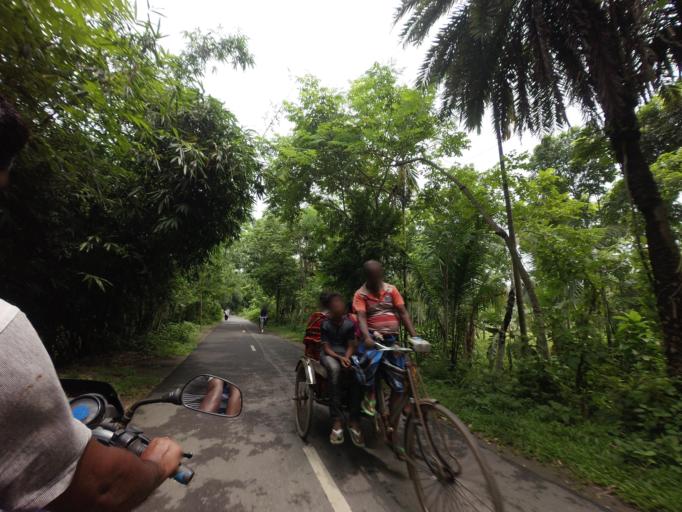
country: BD
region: Khulna
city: Kalia
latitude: 23.0884
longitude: 89.6605
